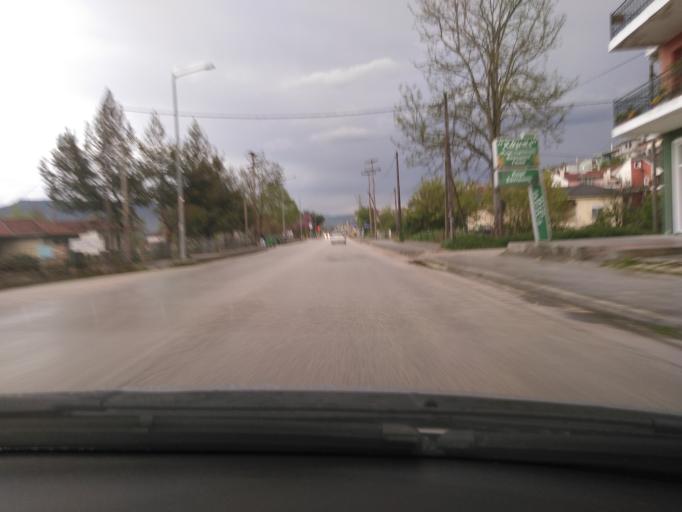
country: GR
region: Epirus
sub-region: Nomos Ioanninon
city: Anatoli
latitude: 39.6310
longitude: 20.8776
